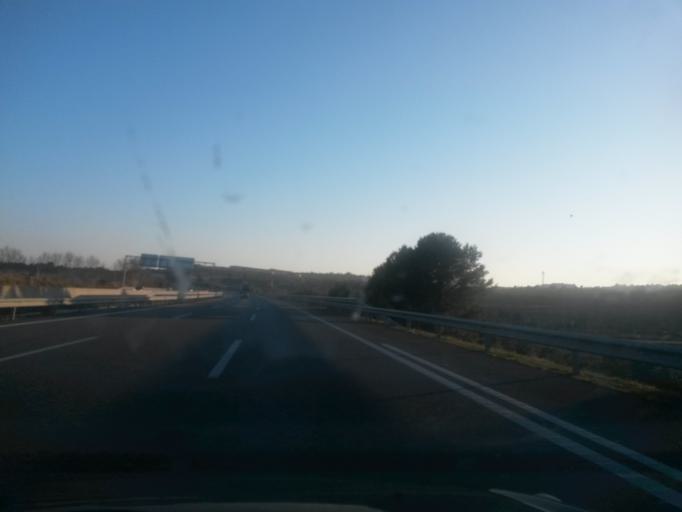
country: ES
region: Catalonia
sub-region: Provincia de Girona
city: Pont de Molins
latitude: 42.2953
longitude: 2.9408
